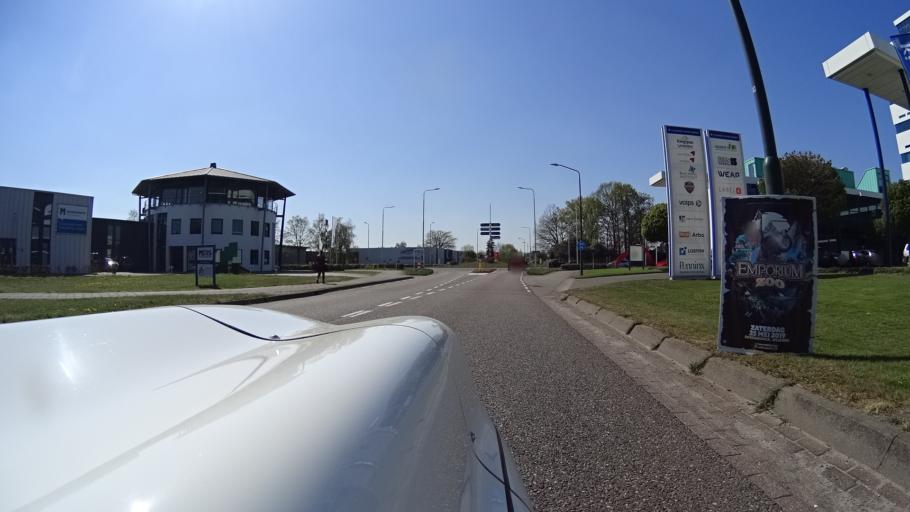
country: NL
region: North Brabant
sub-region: Gemeente Boekel
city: Boekel
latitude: 51.5661
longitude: 5.7107
